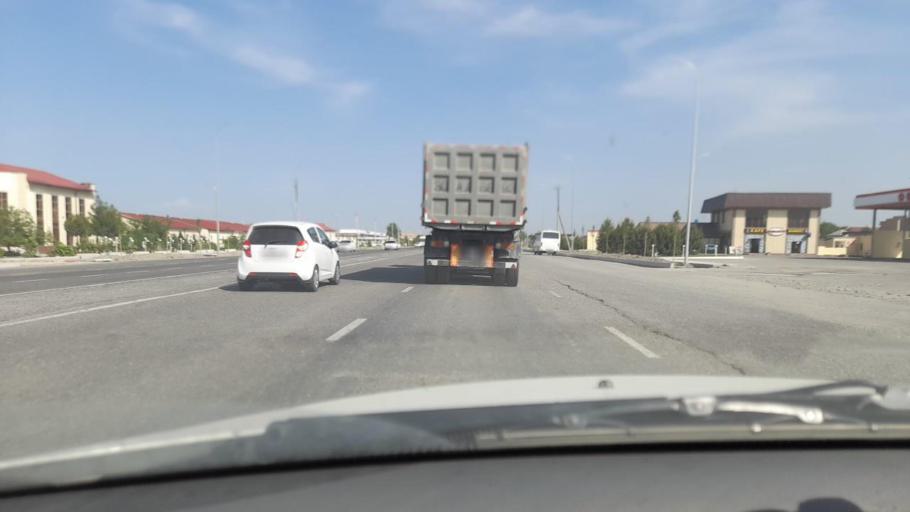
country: UZ
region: Samarqand
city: Daxbet
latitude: 39.7303
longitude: 66.9388
